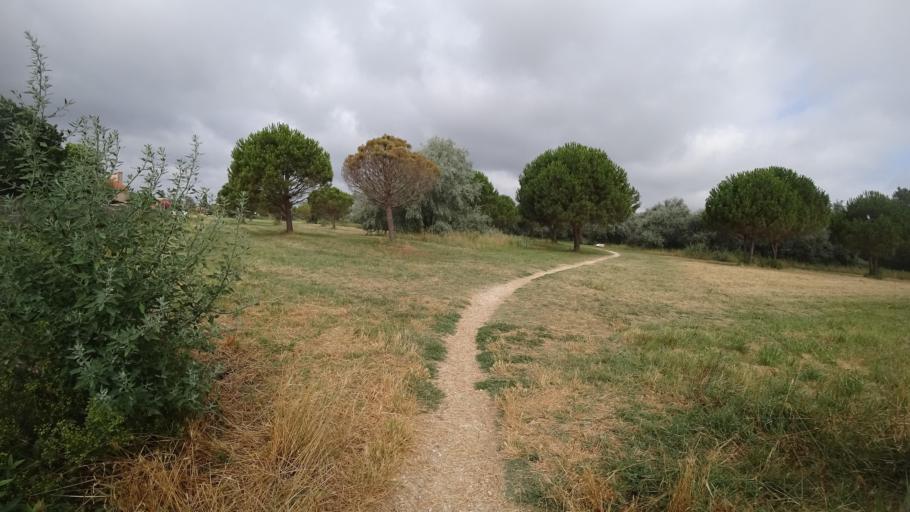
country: FR
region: Languedoc-Roussillon
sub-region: Departement des Pyrenees-Orientales
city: Sainte-Marie-Plage
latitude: 42.7359
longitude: 3.0280
